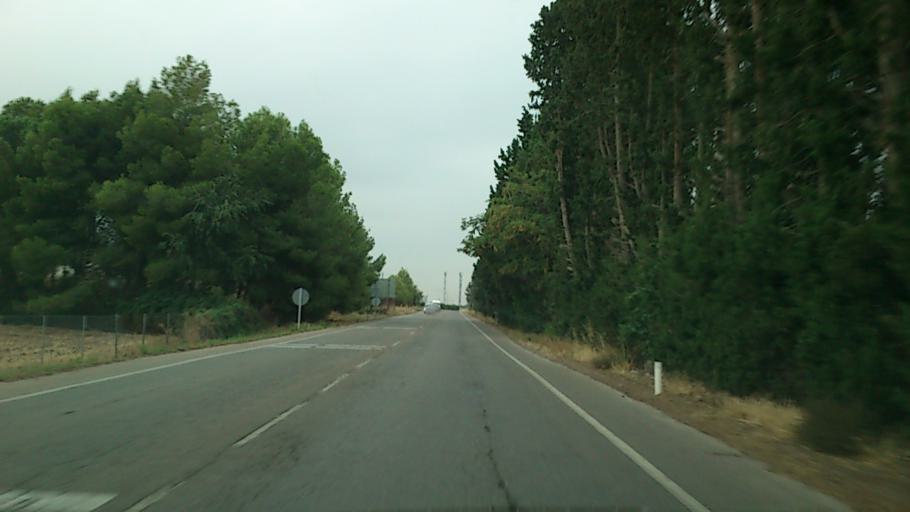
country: ES
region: Aragon
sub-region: Provincia de Zaragoza
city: Villanueva de Gallego
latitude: 41.7228
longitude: -0.8108
